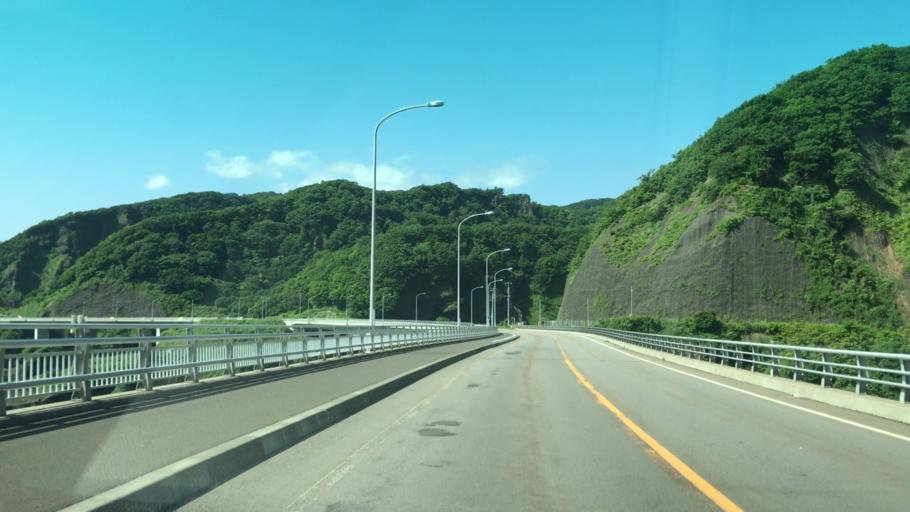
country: JP
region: Hokkaido
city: Iwanai
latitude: 43.1247
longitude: 140.4428
